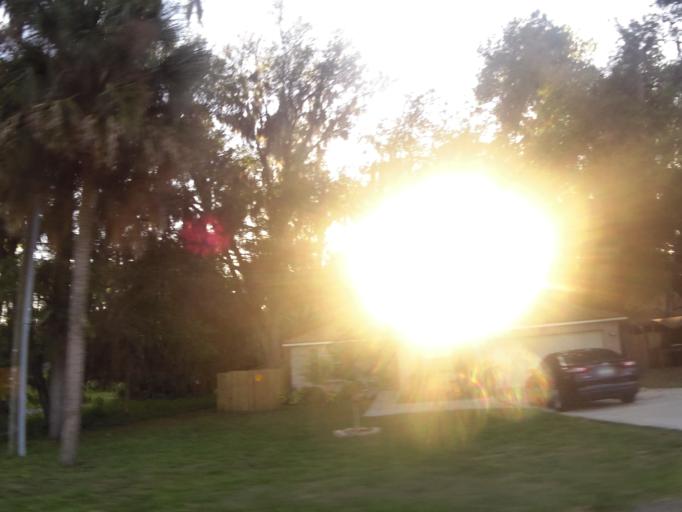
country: US
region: Florida
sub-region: Duval County
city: Atlantic Beach
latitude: 30.3644
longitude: -81.5156
